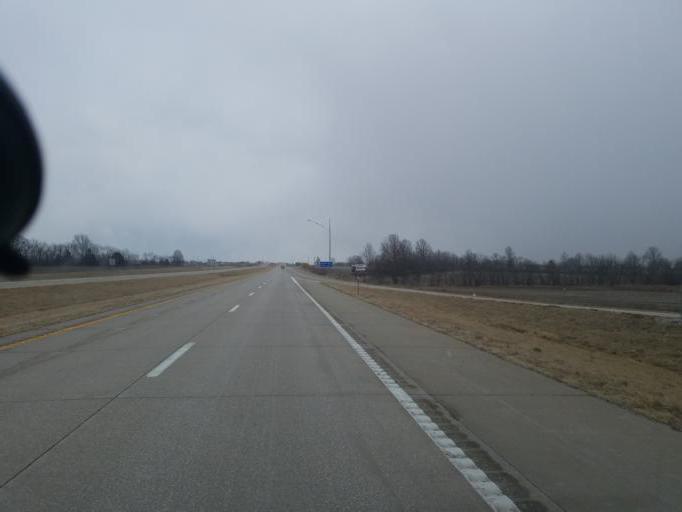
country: US
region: Missouri
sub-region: Randolph County
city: Moberly
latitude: 39.4532
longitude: -92.4309
